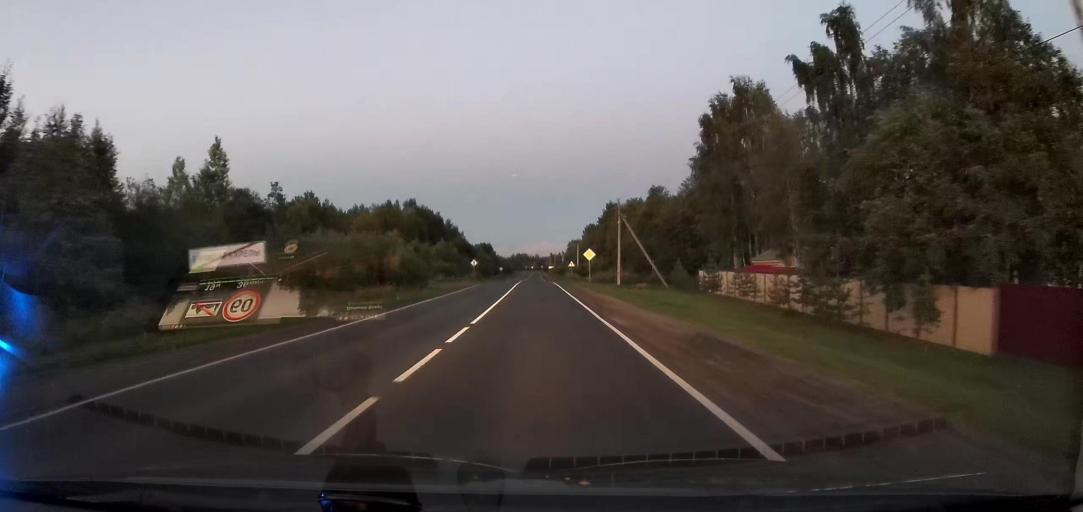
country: RU
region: Arkhangelskaya
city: Uyemskiy
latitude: 64.4447
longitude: 40.9505
